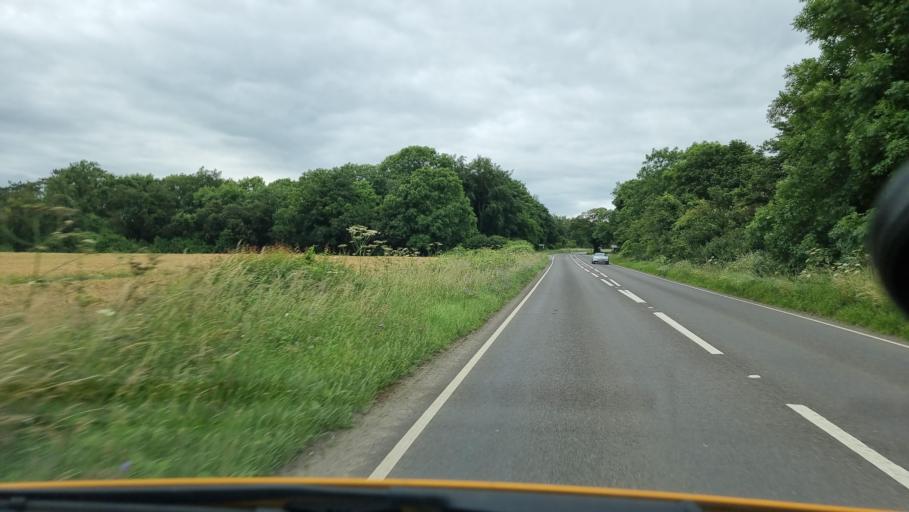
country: GB
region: England
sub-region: Oxfordshire
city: Woodstock
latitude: 51.8973
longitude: -1.3280
